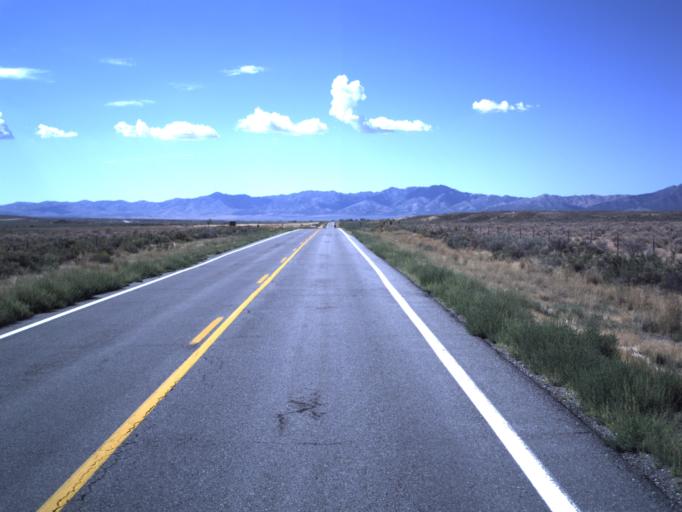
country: US
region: Utah
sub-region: Tooele County
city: Tooele
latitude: 40.2035
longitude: -112.4108
